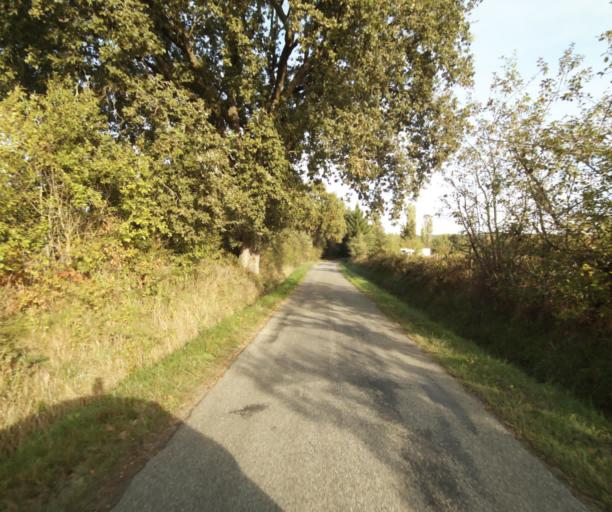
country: FR
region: Midi-Pyrenees
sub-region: Departement de la Haute-Garonne
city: Villemur-sur-Tarn
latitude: 43.9248
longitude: 1.5050
